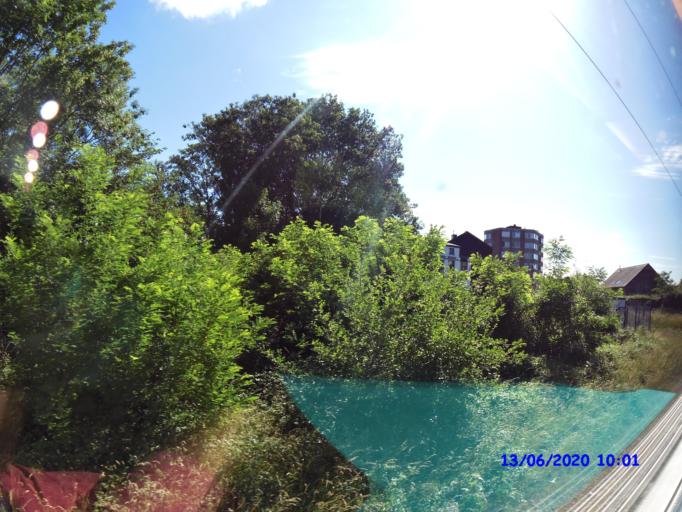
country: BE
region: Wallonia
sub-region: Province de Liege
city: Liege
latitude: 50.6458
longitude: 5.5505
